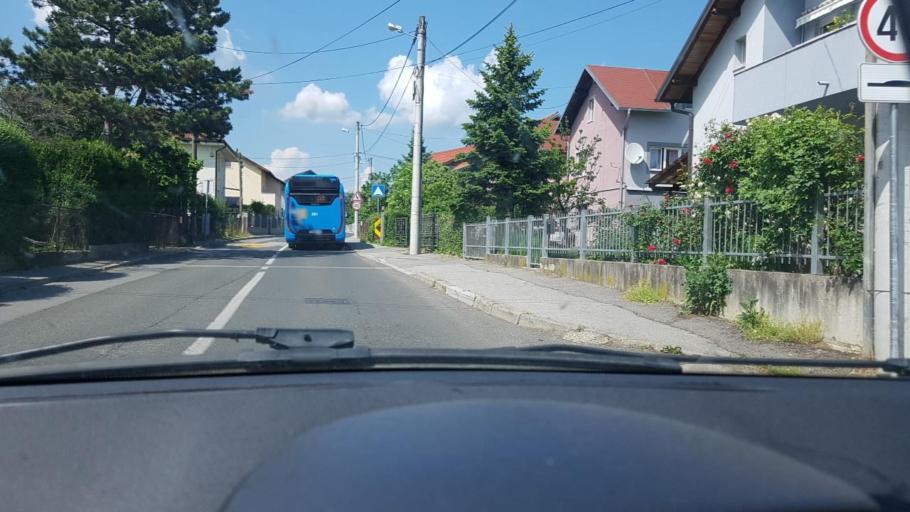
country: HR
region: Grad Zagreb
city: Zagreb
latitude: 45.8387
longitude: 16.0080
